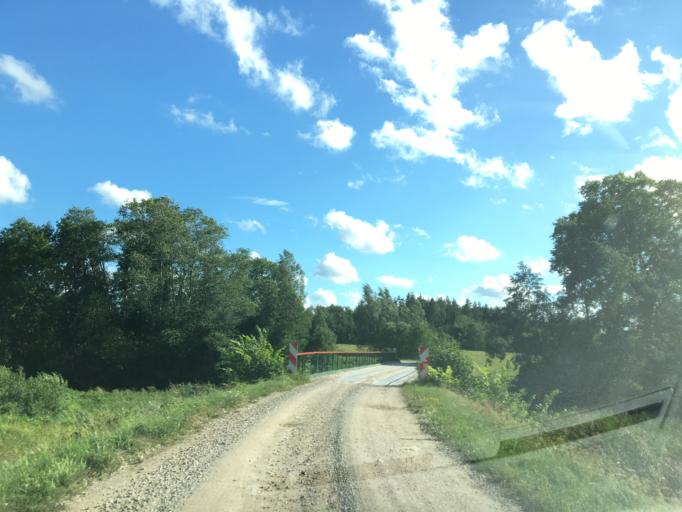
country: EE
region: Viljandimaa
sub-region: Suure-Jaani vald
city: Suure-Jaani
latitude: 58.5808
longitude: 25.2722
